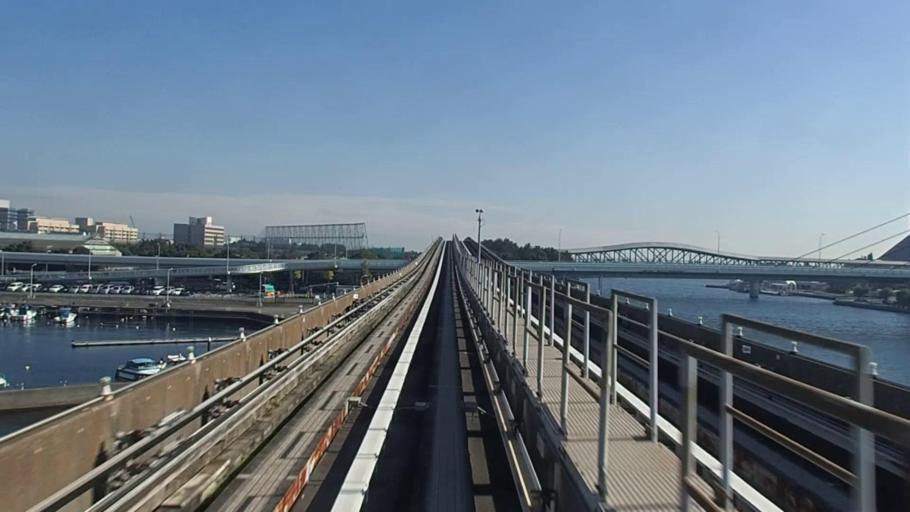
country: JP
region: Kanagawa
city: Yokosuka
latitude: 35.3401
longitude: 139.6426
